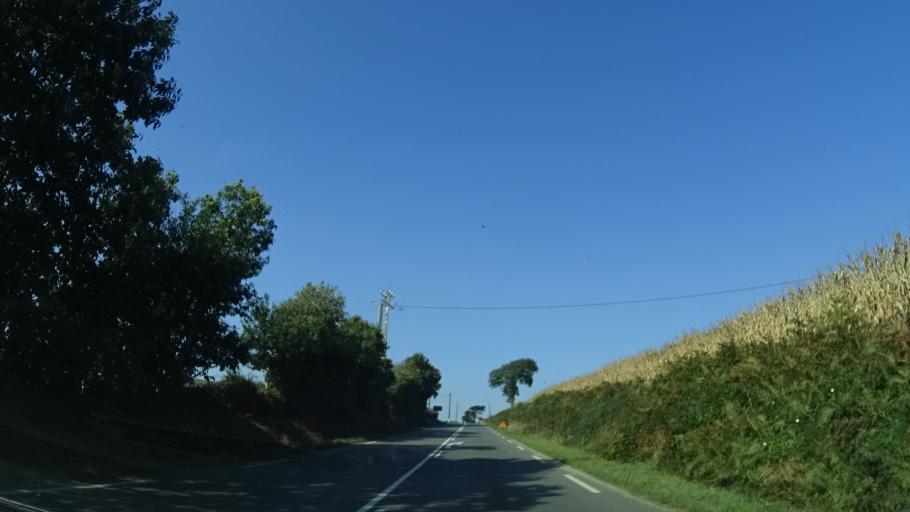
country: FR
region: Brittany
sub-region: Departement du Finistere
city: Plonevez-Porzay
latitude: 48.1145
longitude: -4.2395
